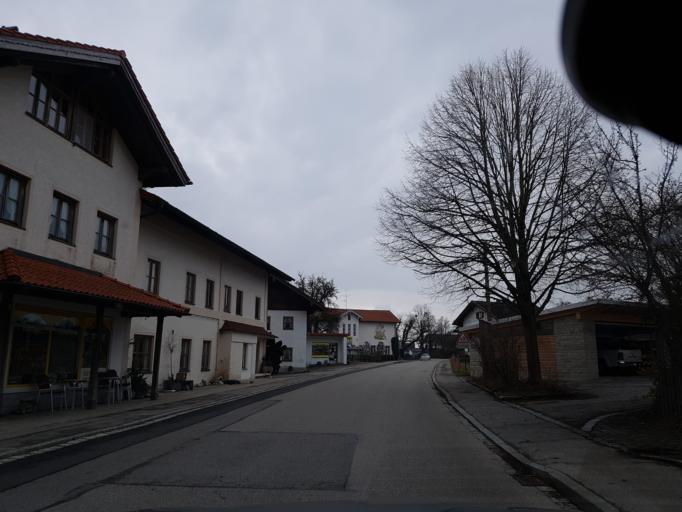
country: DE
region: Bavaria
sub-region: Upper Bavaria
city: Bruckmuhl
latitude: 47.9266
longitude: 11.8993
